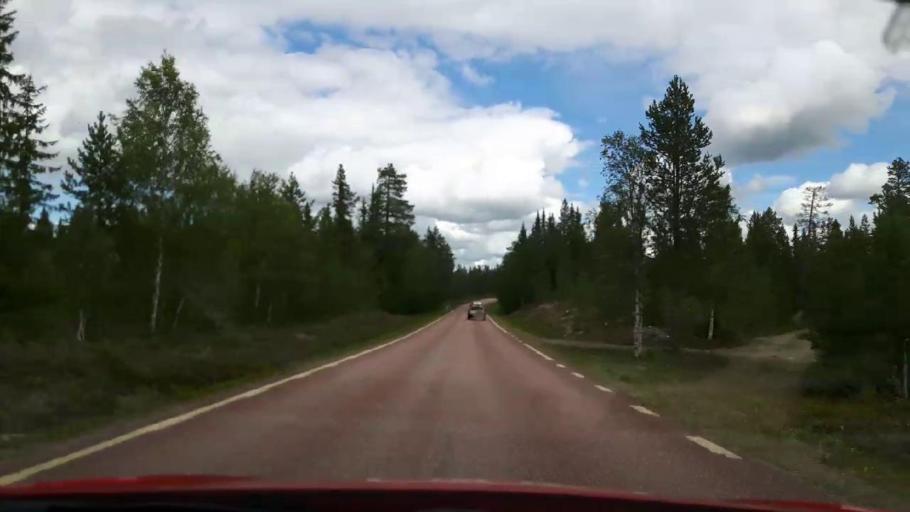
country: NO
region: Hedmark
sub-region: Trysil
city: Innbygda
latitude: 61.8786
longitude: 12.9689
